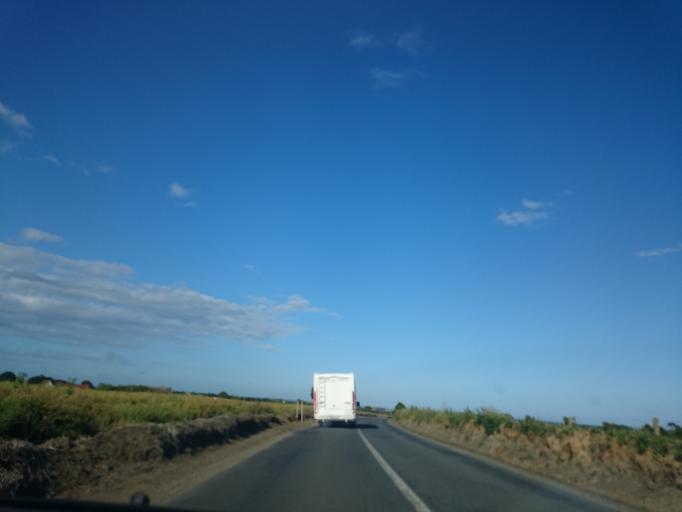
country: IE
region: Leinster
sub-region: Loch Garman
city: Loch Garman
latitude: 52.1877
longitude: -6.5654
